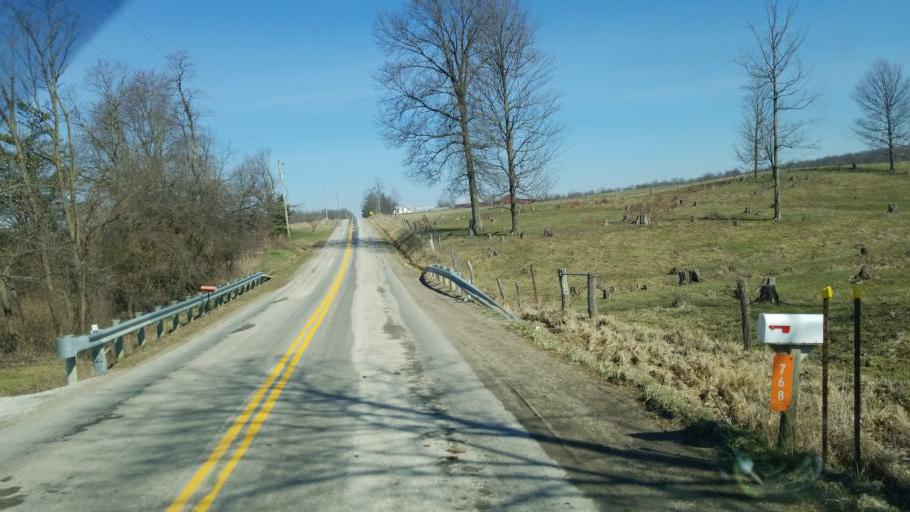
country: US
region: Ohio
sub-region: Ashland County
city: Ashland
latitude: 40.9494
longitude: -82.2436
